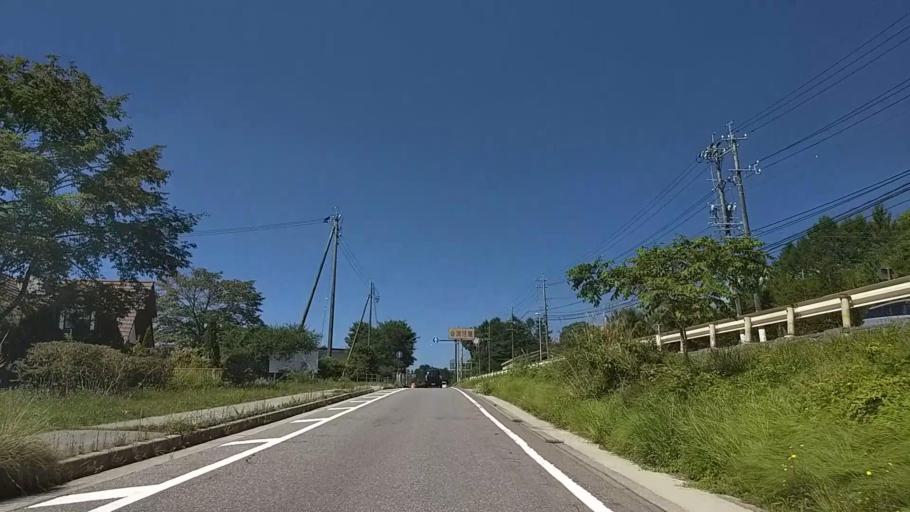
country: JP
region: Nagano
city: Komoro
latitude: 36.3429
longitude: 138.5688
